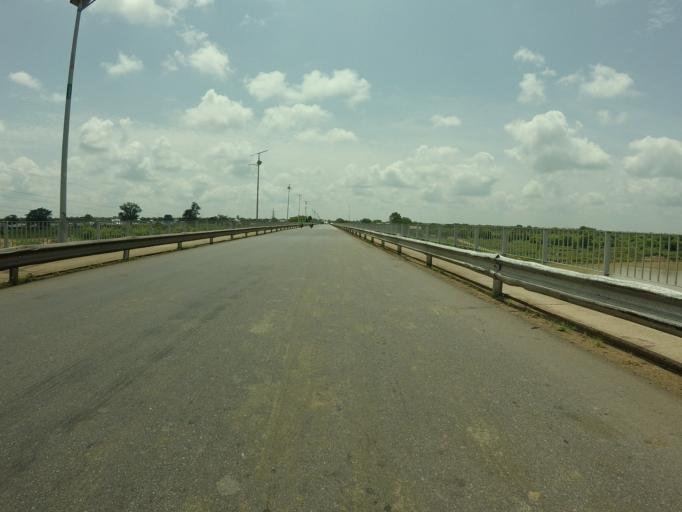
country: GH
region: Northern
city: Tamale
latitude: 9.1402
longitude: -1.1609
